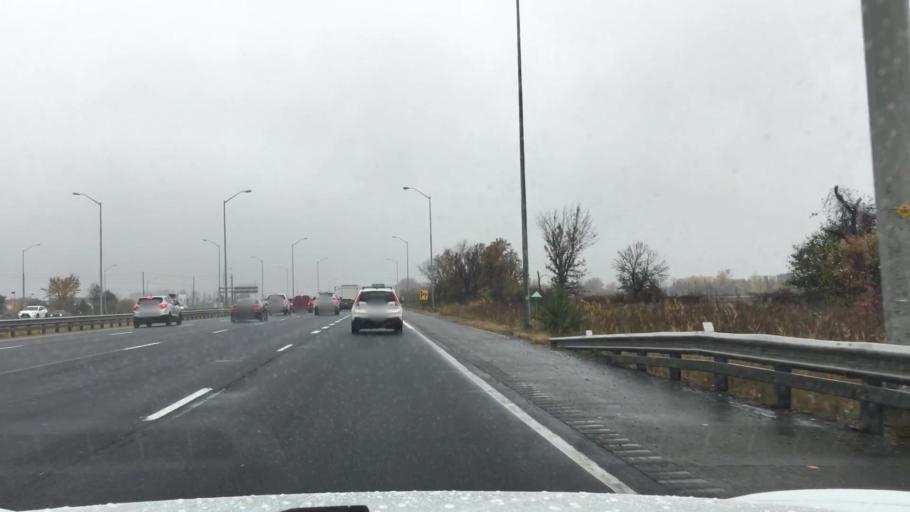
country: CA
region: Ontario
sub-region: York
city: Richmond Hill
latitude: 43.8616
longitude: -79.3742
